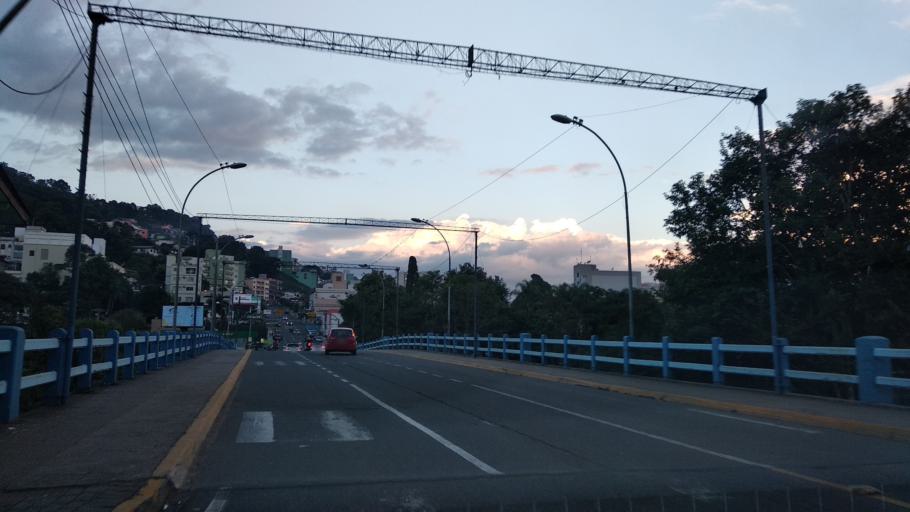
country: BR
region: Santa Catarina
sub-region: Videira
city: Videira
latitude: -27.0058
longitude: -51.1559
